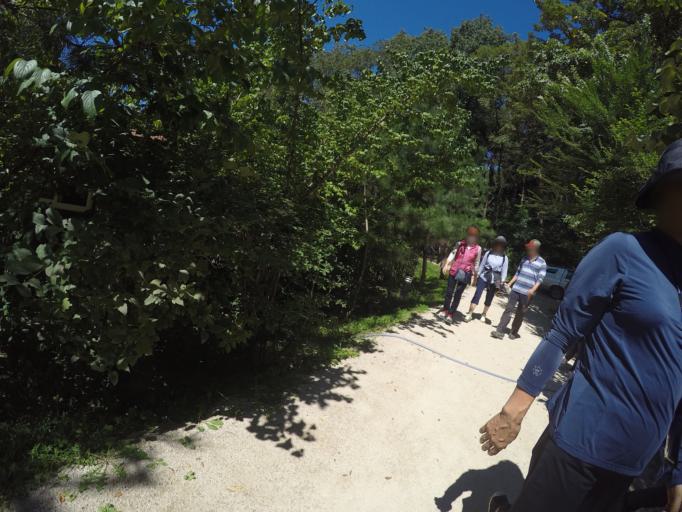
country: KR
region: Seoul
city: Seoul
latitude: 37.5073
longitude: 127.0479
